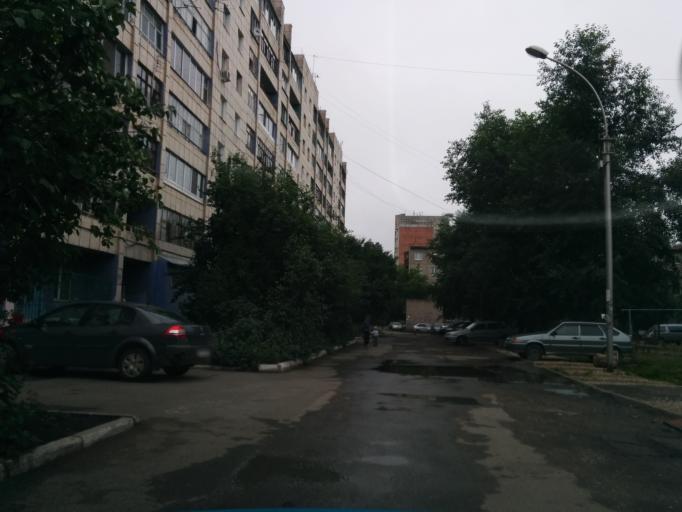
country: RU
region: Perm
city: Kondratovo
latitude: 58.0286
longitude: 56.0061
